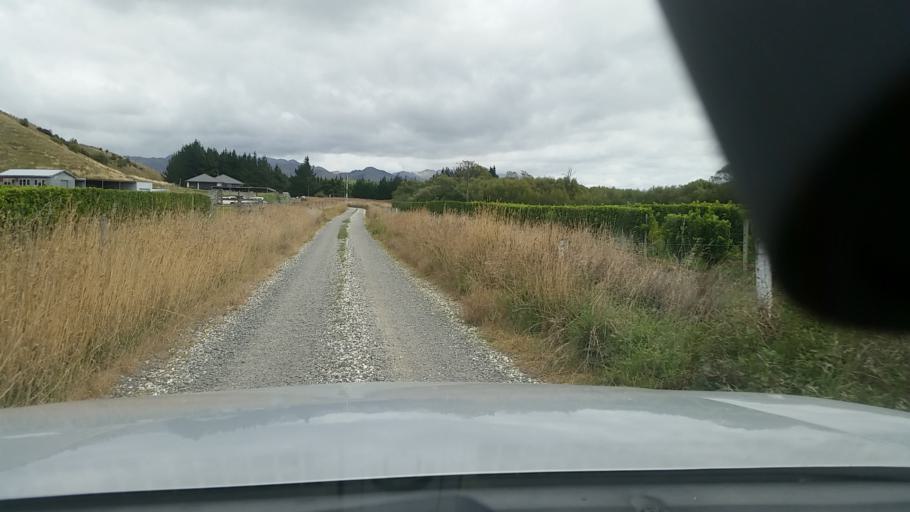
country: NZ
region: Marlborough
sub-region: Marlborough District
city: Blenheim
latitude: -41.6973
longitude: 174.1217
